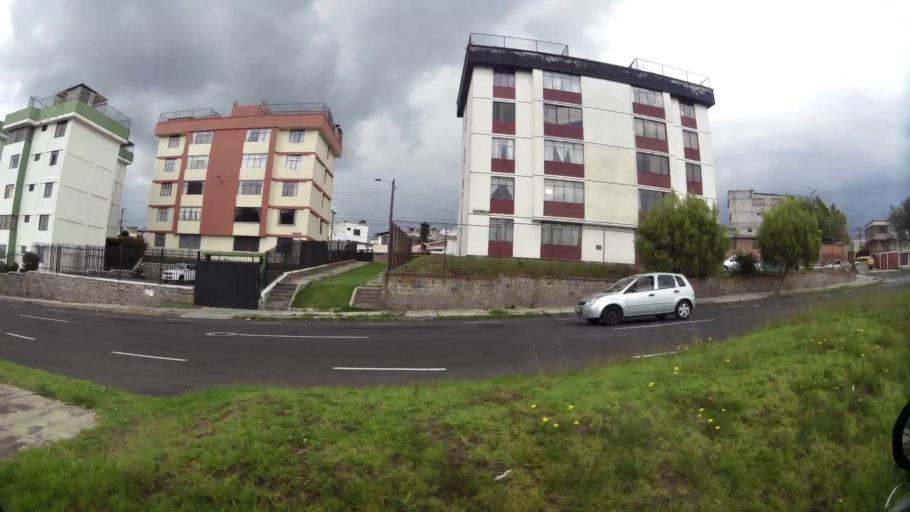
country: EC
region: Pichincha
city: Quito
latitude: -0.0847
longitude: -78.4722
